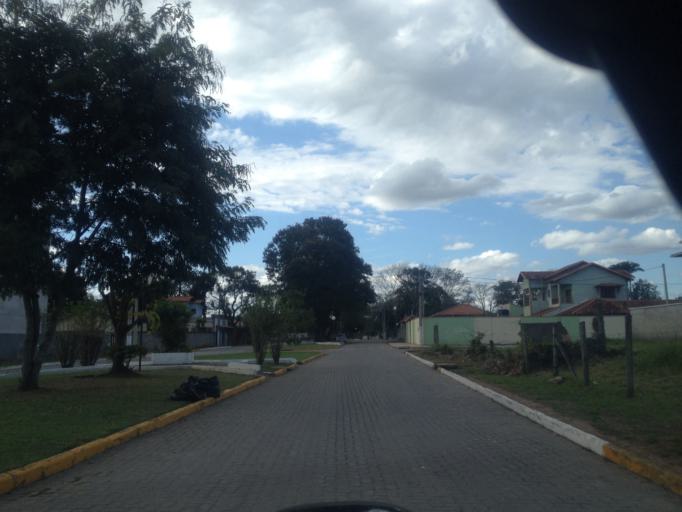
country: BR
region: Rio de Janeiro
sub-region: Porto Real
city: Porto Real
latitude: -22.4210
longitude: -44.2941
